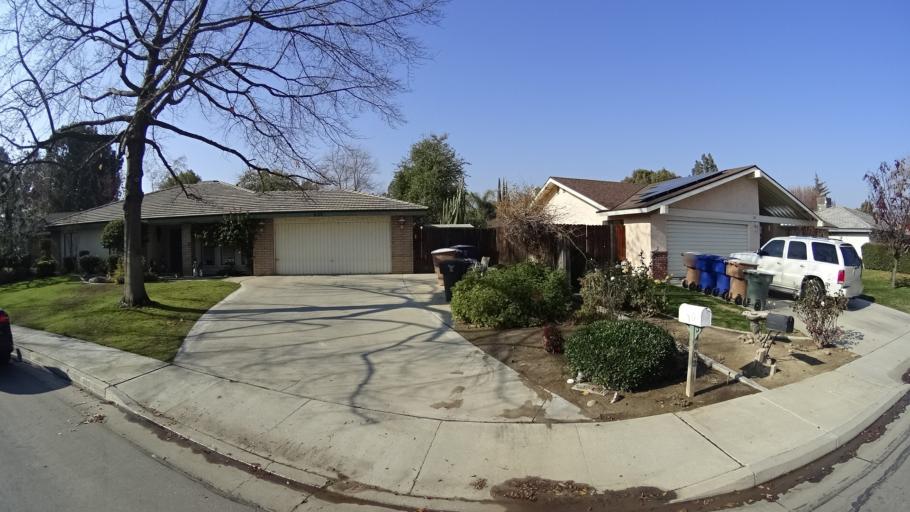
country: US
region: California
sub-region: Kern County
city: Greenacres
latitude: 35.3588
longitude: -119.0859
